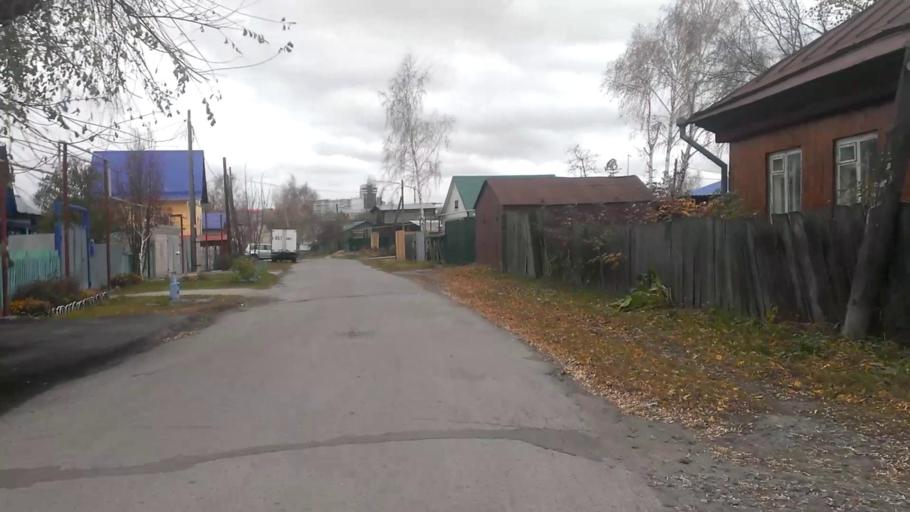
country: RU
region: Altai Krai
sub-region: Gorod Barnaulskiy
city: Barnaul
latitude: 53.3517
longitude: 83.7470
